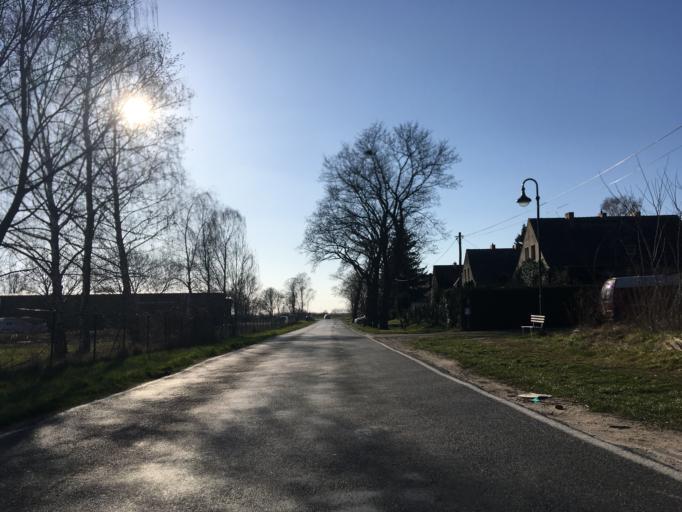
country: DE
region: Brandenburg
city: Ahrensfelde
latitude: 52.6263
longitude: 13.5723
